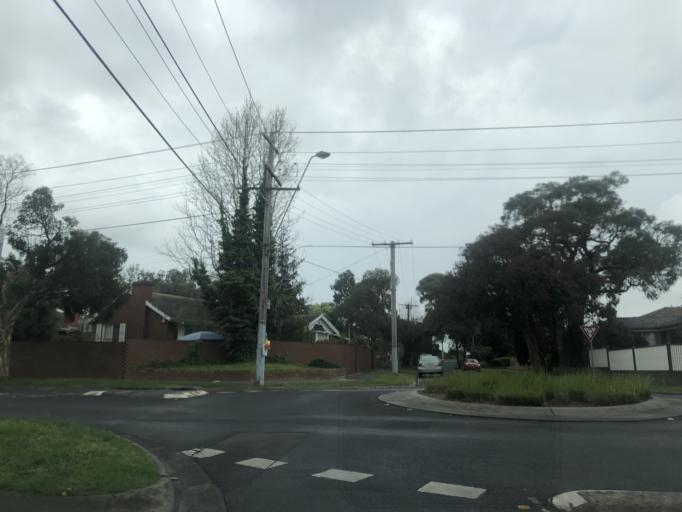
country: AU
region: Victoria
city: Burwood East
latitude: -37.8610
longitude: 145.1385
